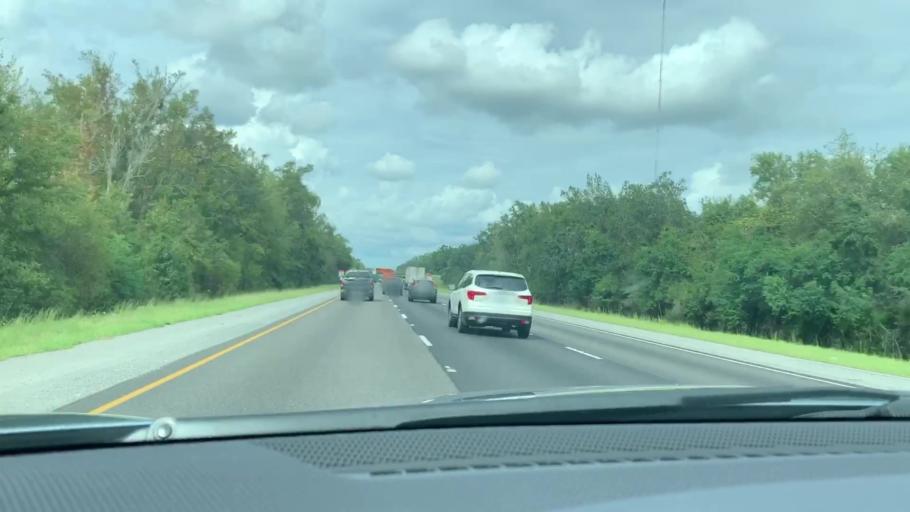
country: US
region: Georgia
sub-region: Liberty County
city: Midway
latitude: 31.6914
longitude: -81.3912
